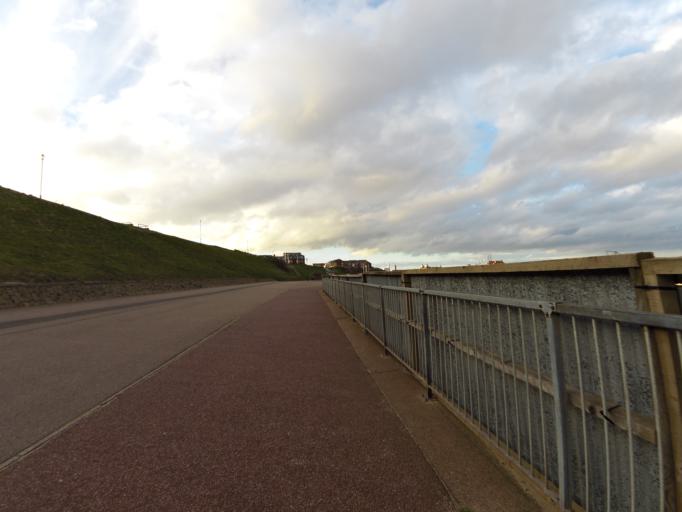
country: GB
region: England
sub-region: Norfolk
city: Gorleston-on-Sea
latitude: 52.5674
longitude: 1.7313
